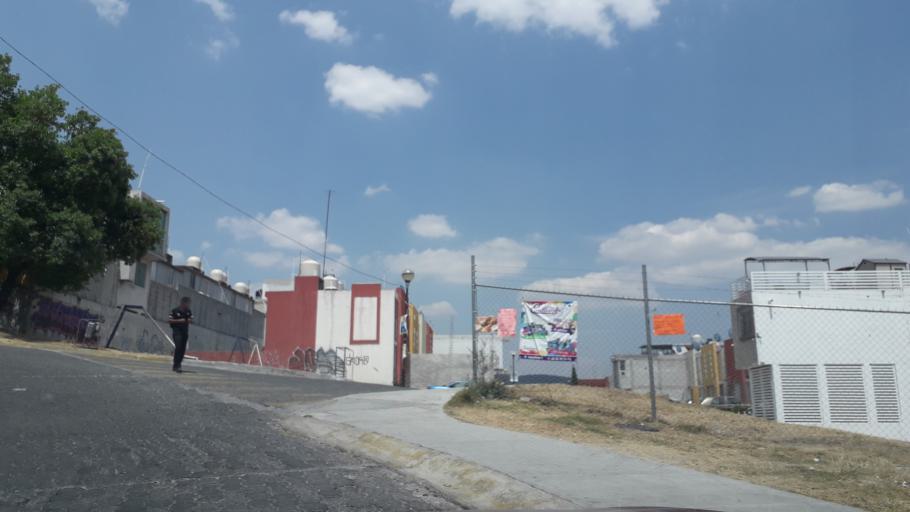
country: MX
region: Puebla
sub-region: Puebla
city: Galaxia la Calera
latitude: 18.9981
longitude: -98.1507
